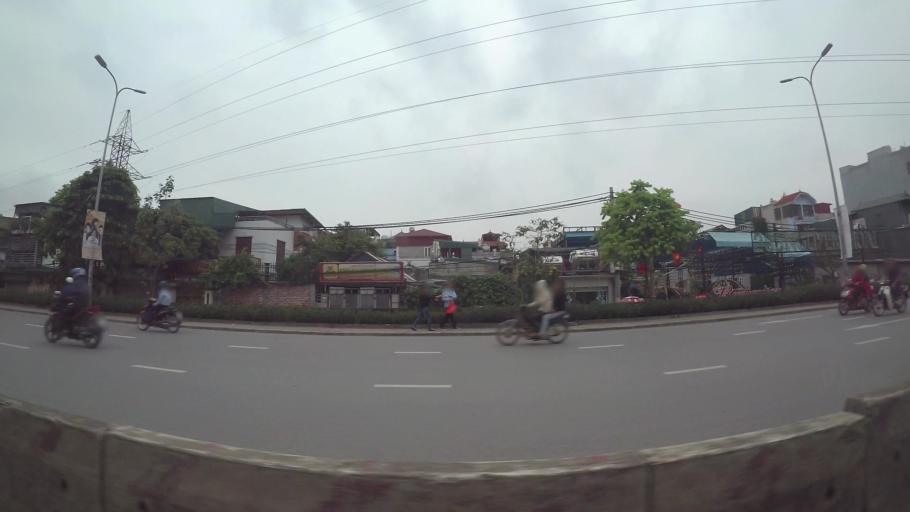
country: VN
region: Ha Noi
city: Hai BaTrung
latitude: 21.0065
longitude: 105.8681
